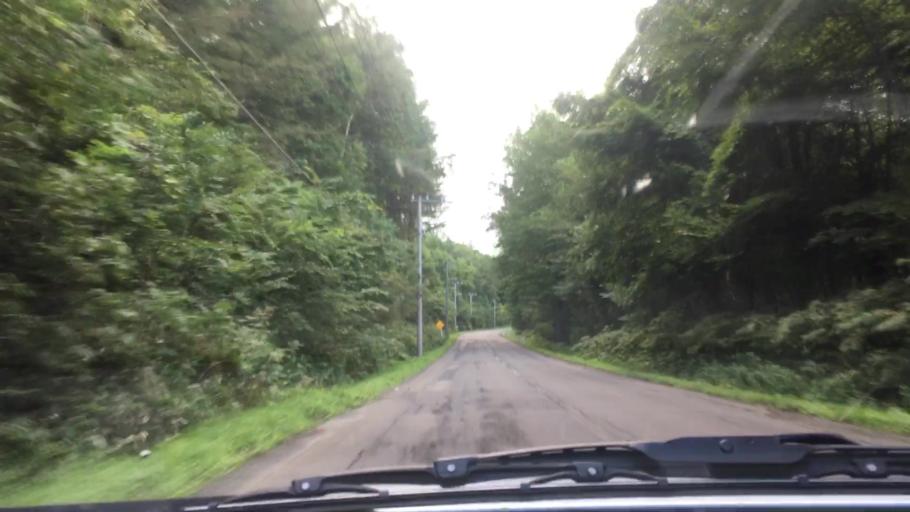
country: JP
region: Hokkaido
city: Otofuke
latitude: 43.1443
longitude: 142.8780
